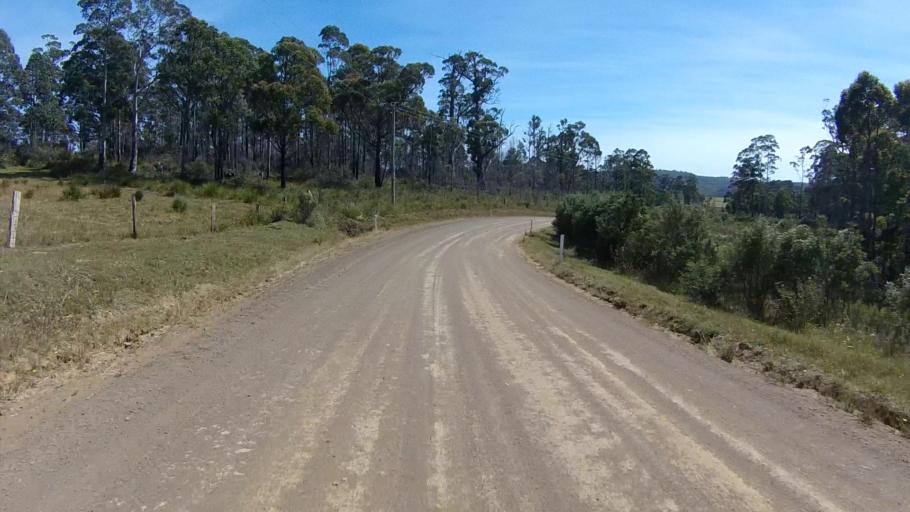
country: AU
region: Tasmania
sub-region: Sorell
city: Sorell
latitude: -42.7293
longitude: 147.7395
